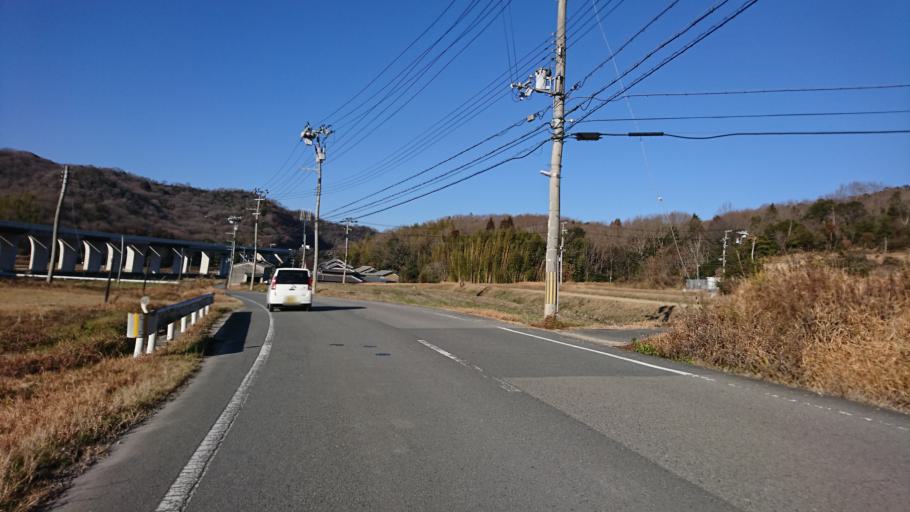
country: JP
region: Hyogo
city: Ono
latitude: 34.8398
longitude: 134.8682
